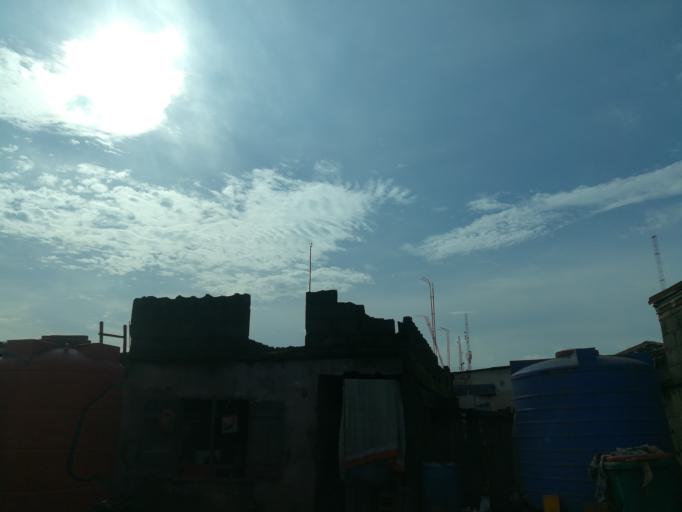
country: NG
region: Lagos
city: Ojota
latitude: 6.6068
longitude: 3.4222
